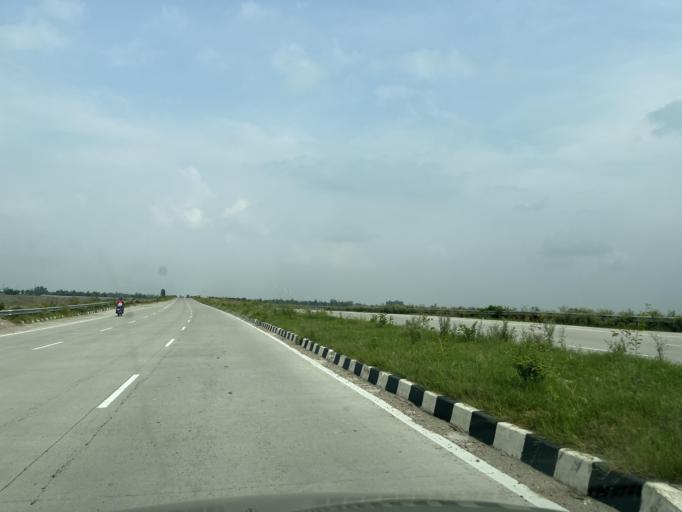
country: IN
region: Uttarakhand
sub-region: Udham Singh Nagar
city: Bazpur
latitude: 29.1466
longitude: 79.0332
